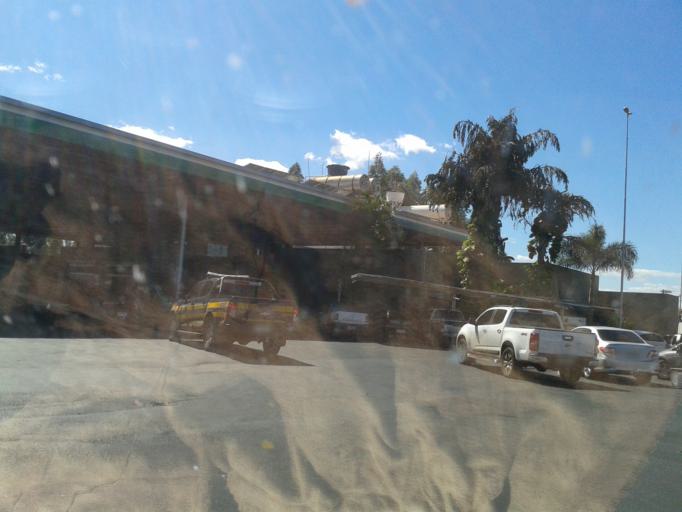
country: BR
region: Goias
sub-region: Itumbiara
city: Itumbiara
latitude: -18.4260
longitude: -49.1924
